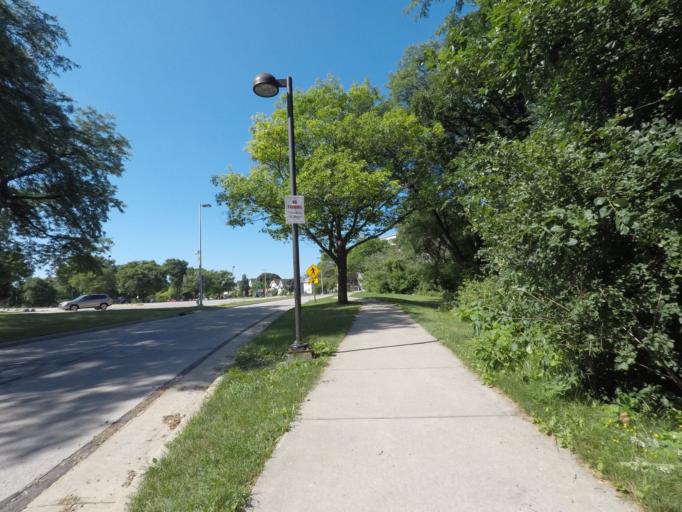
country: US
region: Wisconsin
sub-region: Milwaukee County
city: West Milwaukee
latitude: 43.0269
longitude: -87.9470
